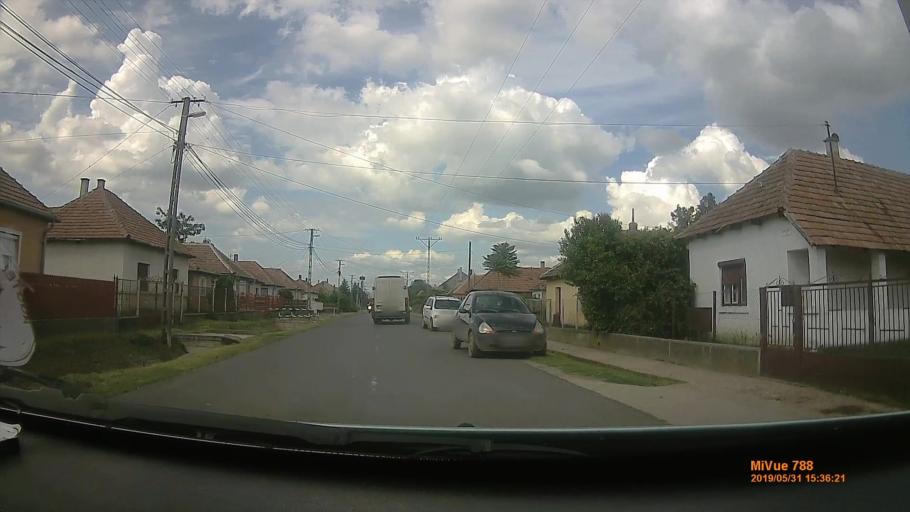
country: HU
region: Borsod-Abauj-Zemplen
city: Prugy
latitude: 48.0833
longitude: 21.2400
